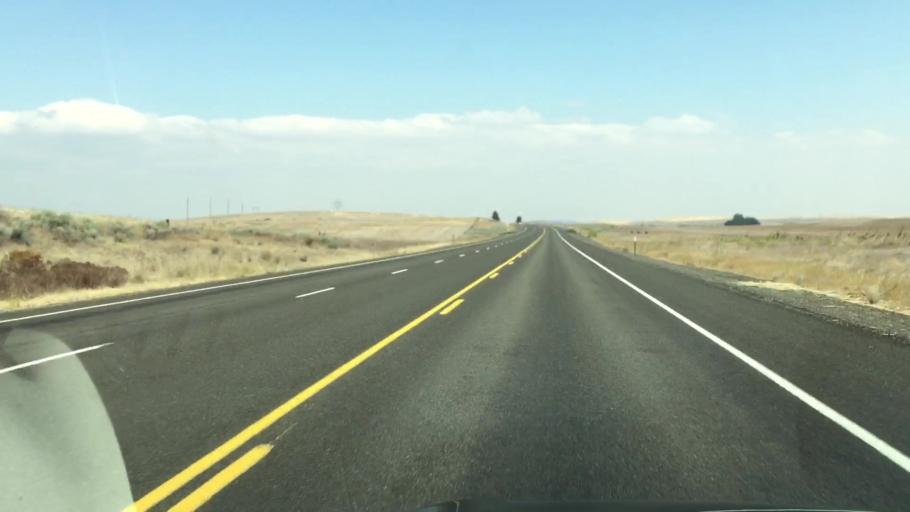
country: US
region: Oregon
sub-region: Wasco County
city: The Dalles
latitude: 45.3995
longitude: -121.1409
